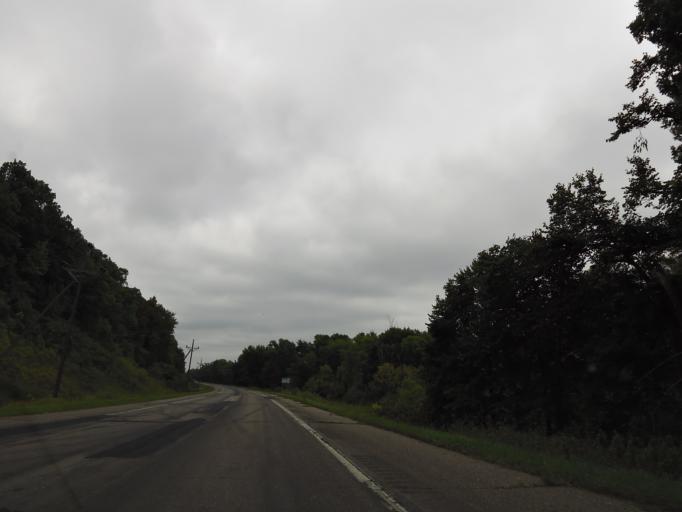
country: US
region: Minnesota
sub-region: Yellow Medicine County
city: Granite Falls
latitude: 44.8627
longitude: -95.6329
